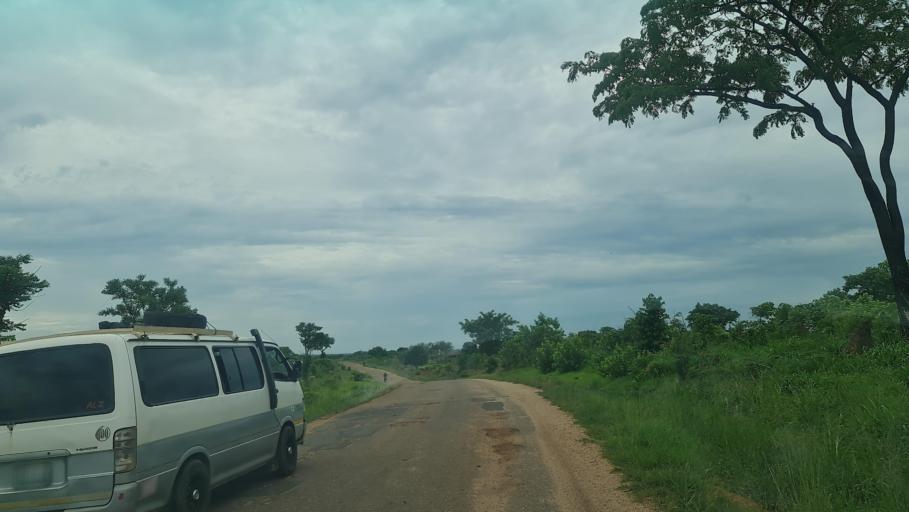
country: MW
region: Southern Region
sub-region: Nsanje District
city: Nsanje
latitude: -17.6842
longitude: 35.7268
